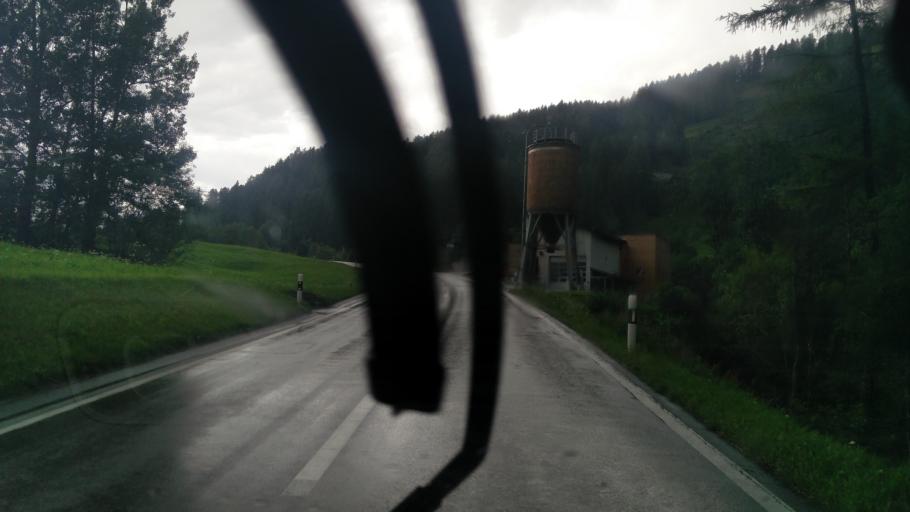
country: IT
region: Trentino-Alto Adige
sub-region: Bolzano
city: Tubre
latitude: 46.6054
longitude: 10.3907
